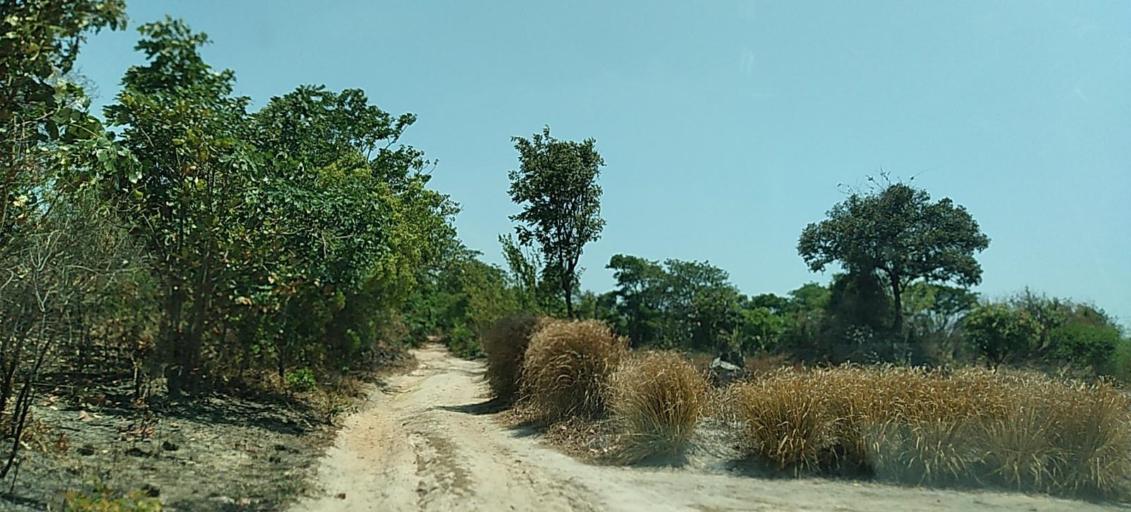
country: ZM
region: Copperbelt
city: Luanshya
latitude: -12.9828
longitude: 28.3295
